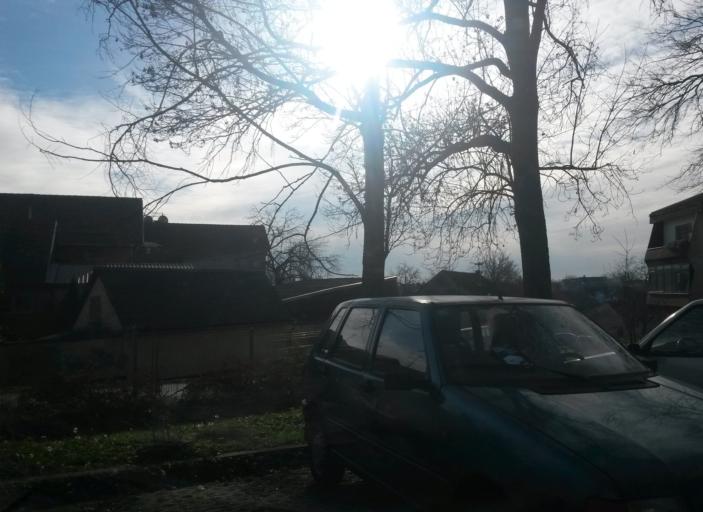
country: HR
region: Osjecko-Baranjska
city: Piskorevci
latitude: 45.3036
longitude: 18.4118
